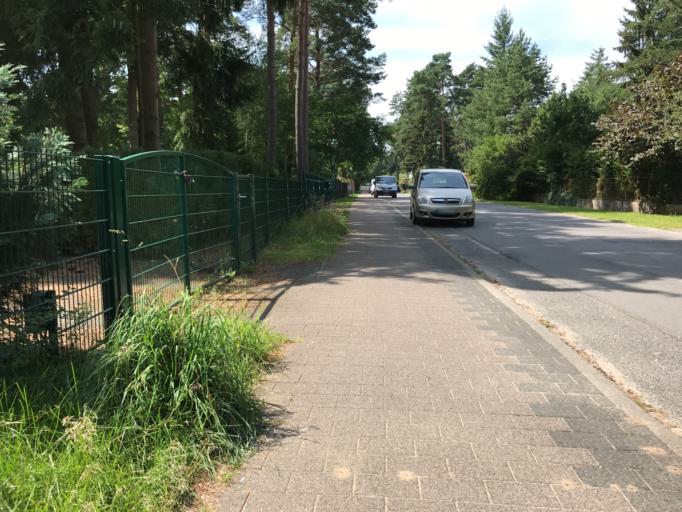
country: DE
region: Brandenburg
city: Wandlitz
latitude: 52.7654
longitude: 13.4582
